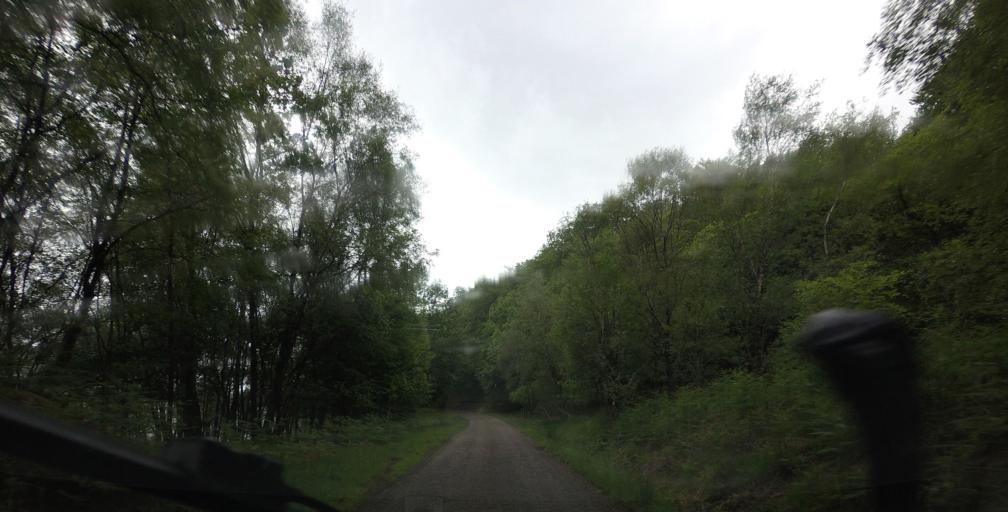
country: GB
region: Scotland
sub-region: Highland
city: Fort William
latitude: 56.7949
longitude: -5.1695
